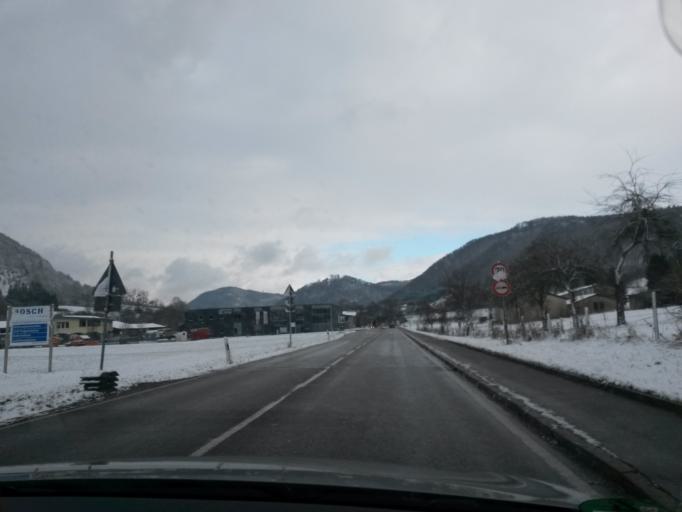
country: DE
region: Baden-Wuerttemberg
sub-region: Regierungsbezirk Stuttgart
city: Muhlhausen
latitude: 48.5791
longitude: 9.6677
